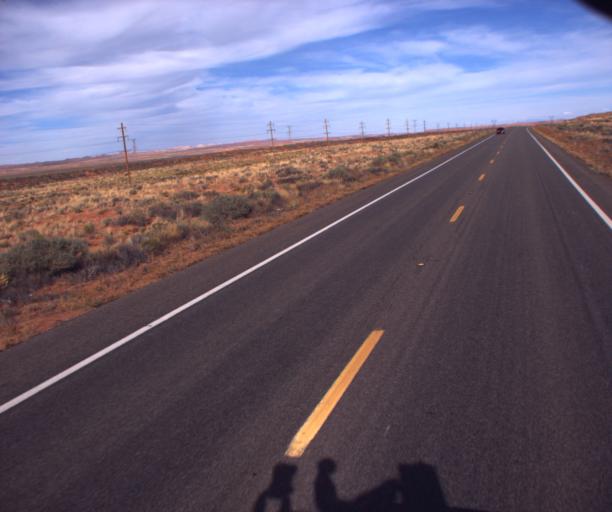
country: US
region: Arizona
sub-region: Navajo County
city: Kayenta
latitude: 36.7929
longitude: -109.9435
